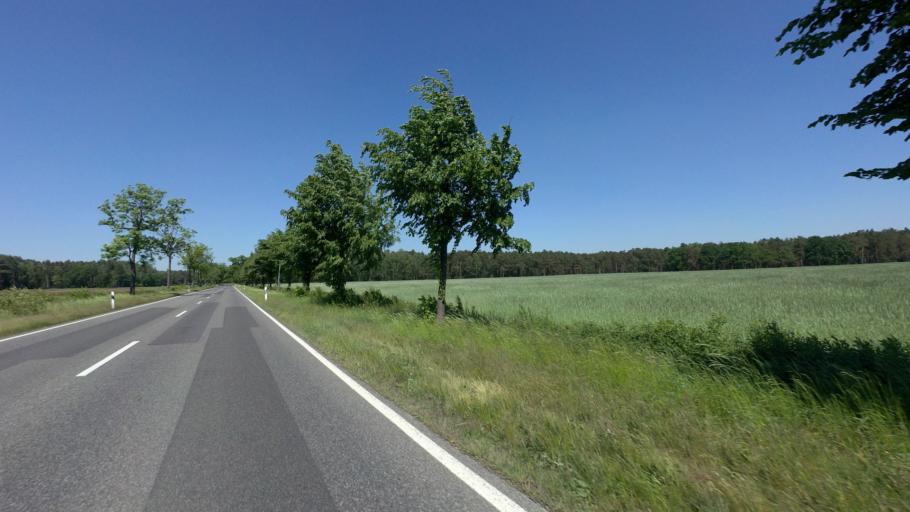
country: DE
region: Brandenburg
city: Drehnow
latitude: 51.8854
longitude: 14.3723
